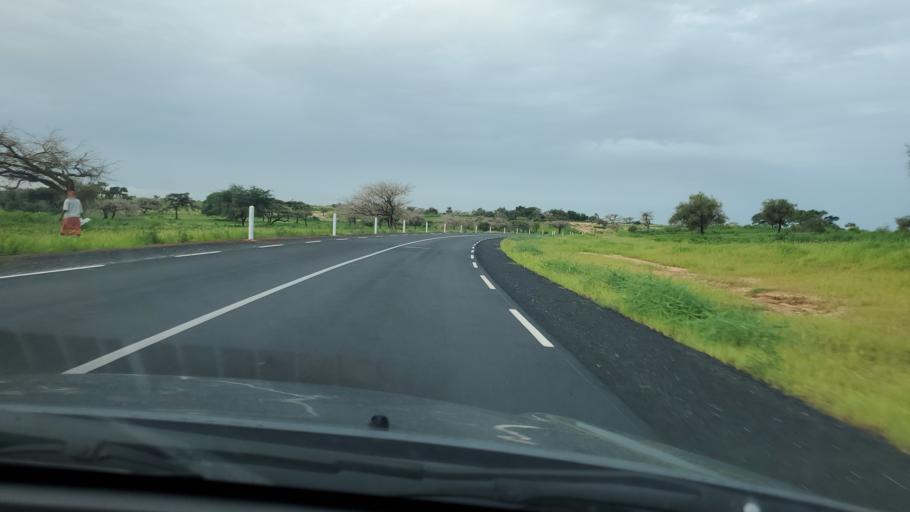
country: SN
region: Louga
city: Gueoul
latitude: 15.6388
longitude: -16.4911
